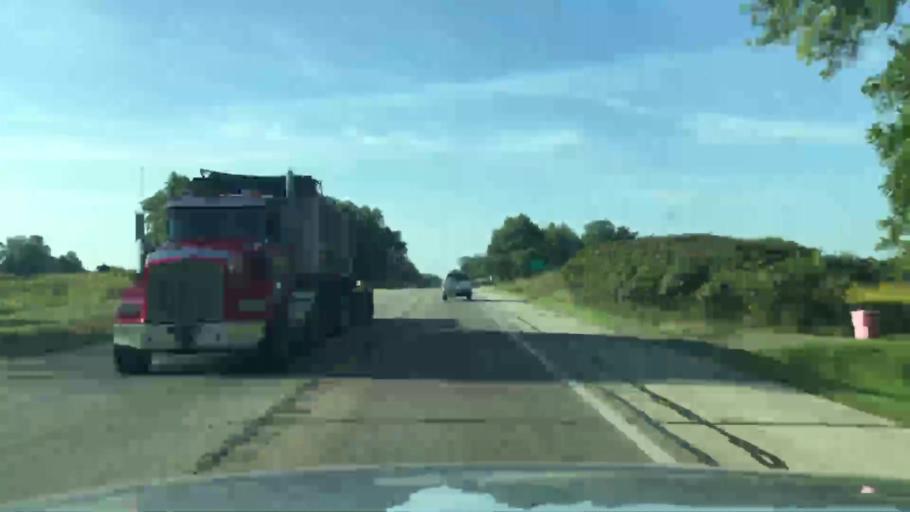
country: US
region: Michigan
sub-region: Jackson County
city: Vandercook Lake
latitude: 42.1058
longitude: -84.3640
